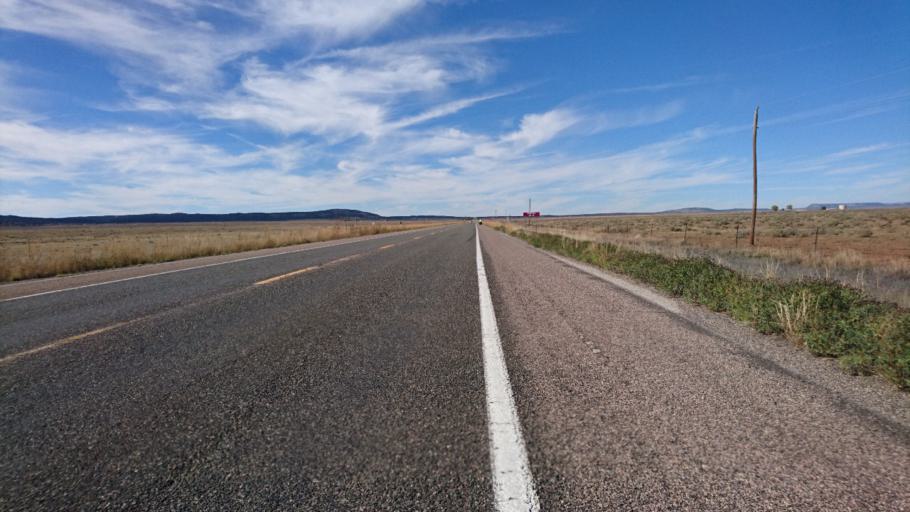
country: US
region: Arizona
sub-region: Mohave County
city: Peach Springs
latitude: 35.4624
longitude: -113.1126
